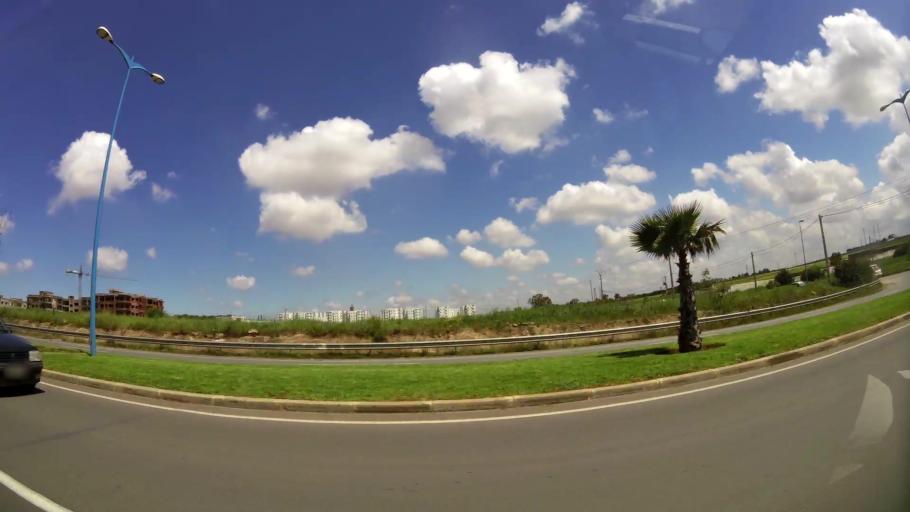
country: MA
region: Grand Casablanca
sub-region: Casablanca
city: Casablanca
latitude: 33.5176
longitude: -7.6150
